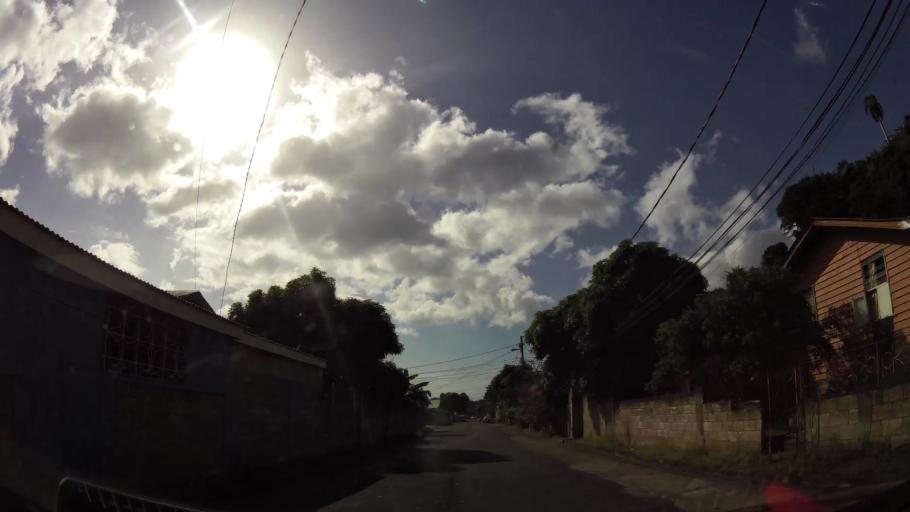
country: DM
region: Saint George
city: Roseau
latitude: 15.3040
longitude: -61.3781
